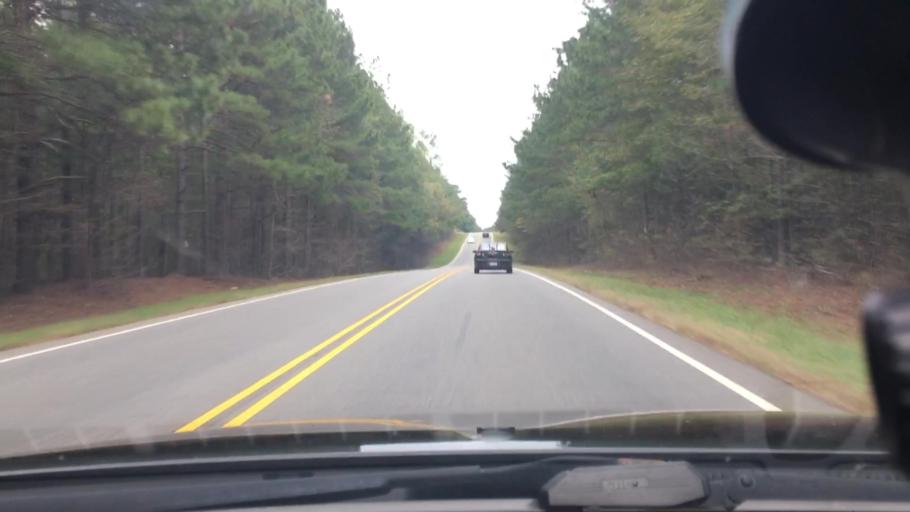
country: US
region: North Carolina
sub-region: Montgomery County
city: Biscoe
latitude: 35.3602
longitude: -79.7139
